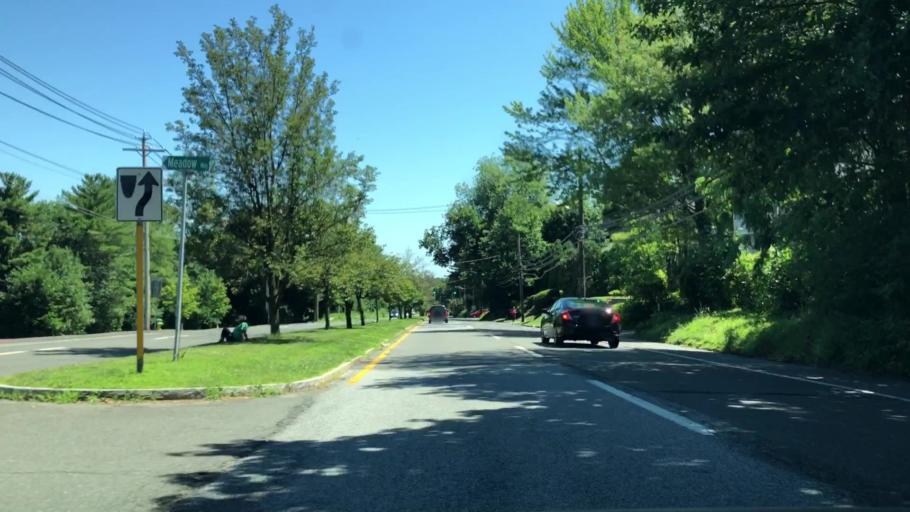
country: US
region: New York
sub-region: Westchester County
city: White Plains
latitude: 41.0008
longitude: -73.7486
